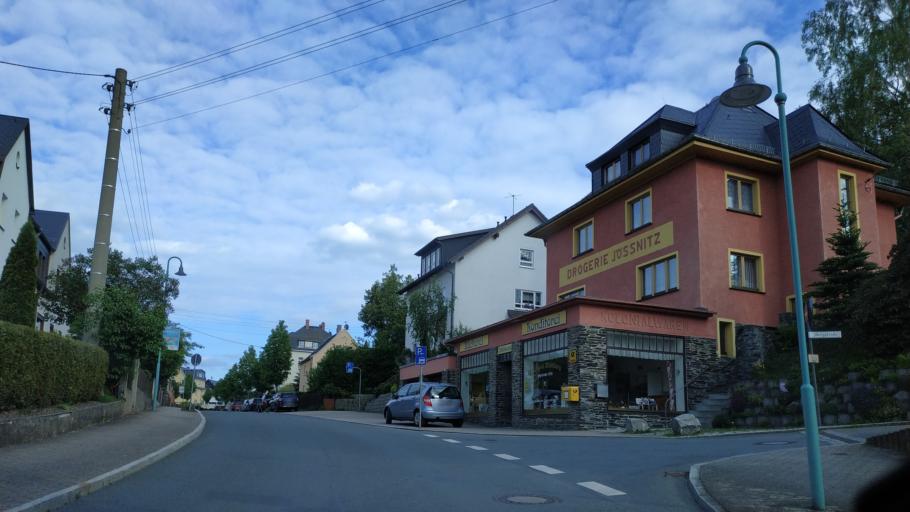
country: DE
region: Saxony
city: Plauen
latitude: 50.5415
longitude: 12.1368
